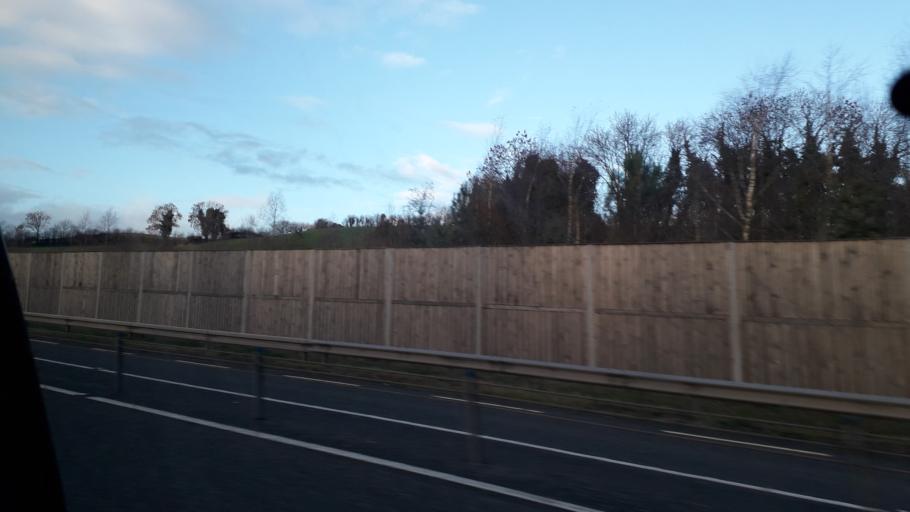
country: IE
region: Ulster
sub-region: County Monaghan
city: Castleblayney
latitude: 54.1472
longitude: -6.7883
